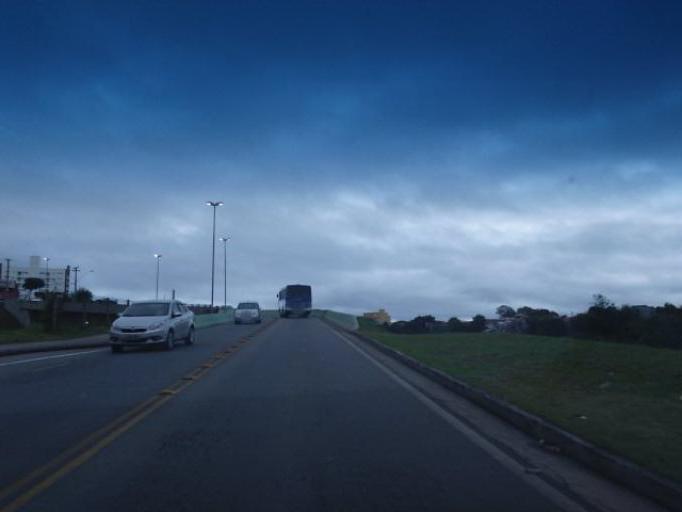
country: BR
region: Sao Paulo
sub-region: Sao Jose Dos Campos
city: Sao Jose dos Campos
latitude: -23.2283
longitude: -45.8775
